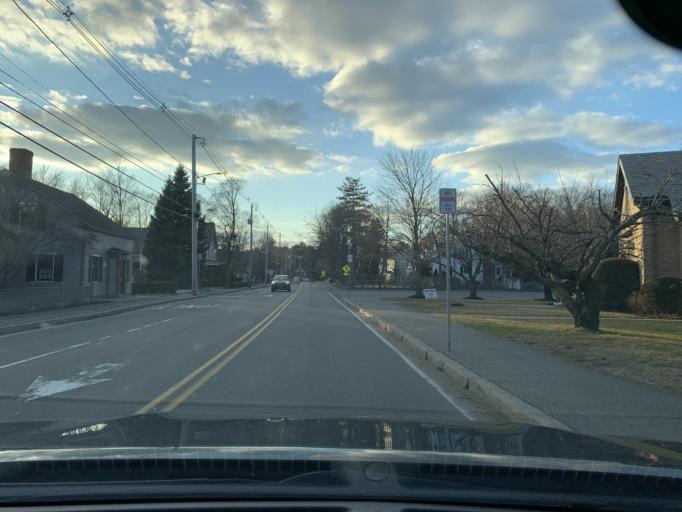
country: US
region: Massachusetts
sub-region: Essex County
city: Lynnfield
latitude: 42.5143
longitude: -71.0050
